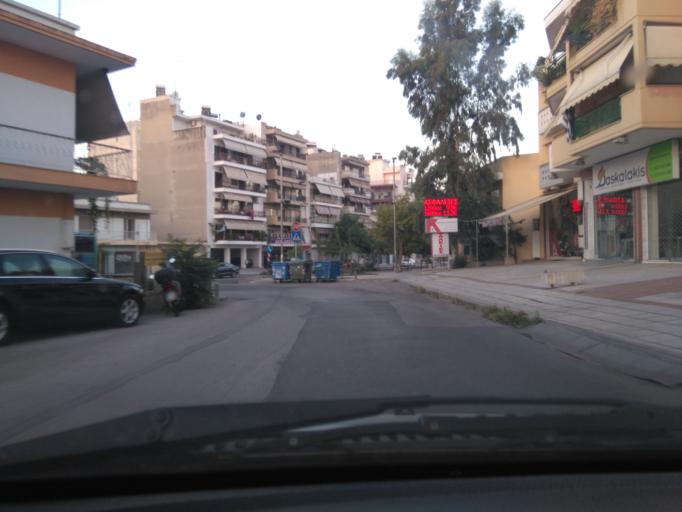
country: GR
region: Central Macedonia
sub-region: Nomos Thessalonikis
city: Stavroupoli
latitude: 40.6635
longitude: 22.9317
